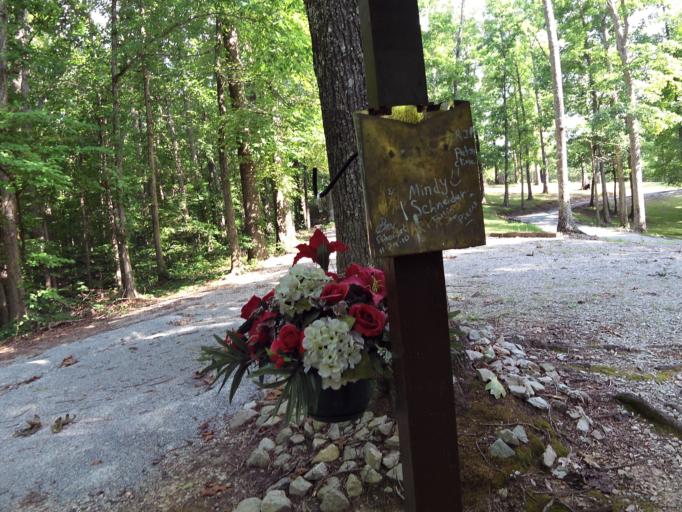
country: US
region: Tennessee
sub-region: Benton County
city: Camden
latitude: 36.0623
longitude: -88.1618
